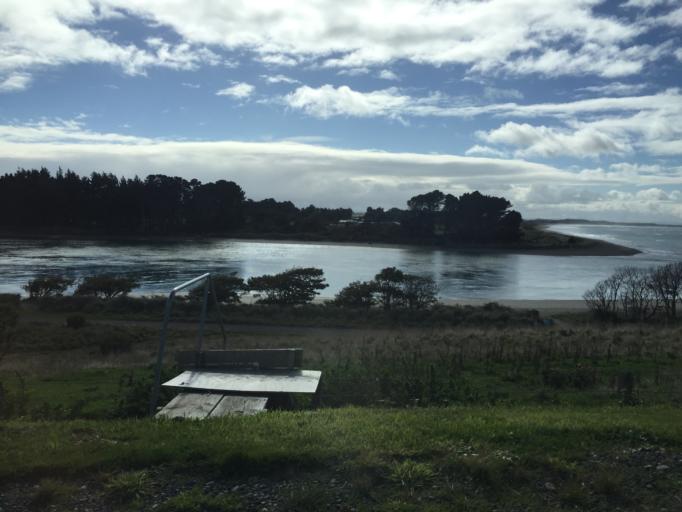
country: NZ
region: Southland
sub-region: Southland District
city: Riverton
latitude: -46.3594
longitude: 168.0189
